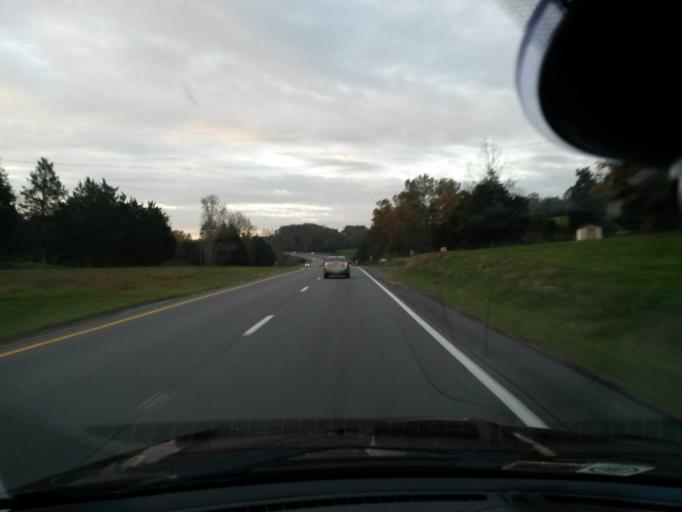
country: US
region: Virginia
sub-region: Botetourt County
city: Fincastle
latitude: 37.5654
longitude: -79.8446
